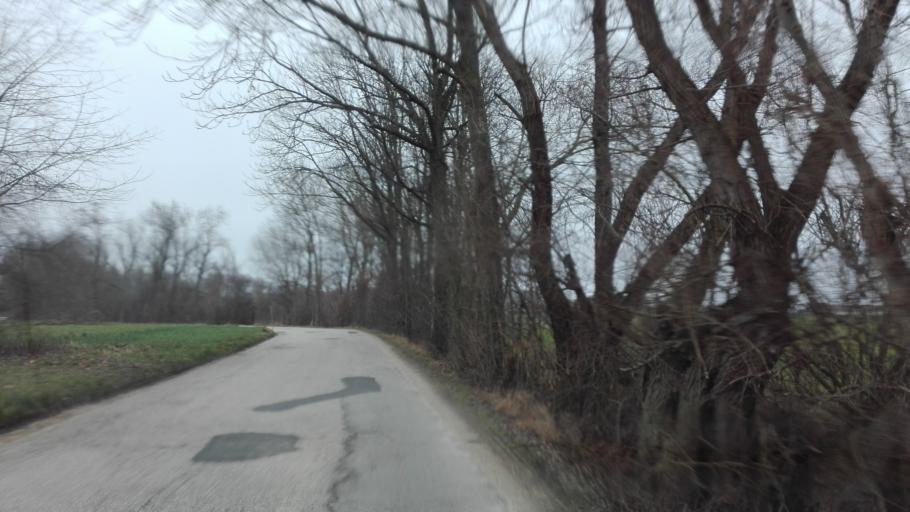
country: AT
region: Upper Austria
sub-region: Politischer Bezirk Linz-Land
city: Horsching
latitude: 48.2419
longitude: 14.1493
